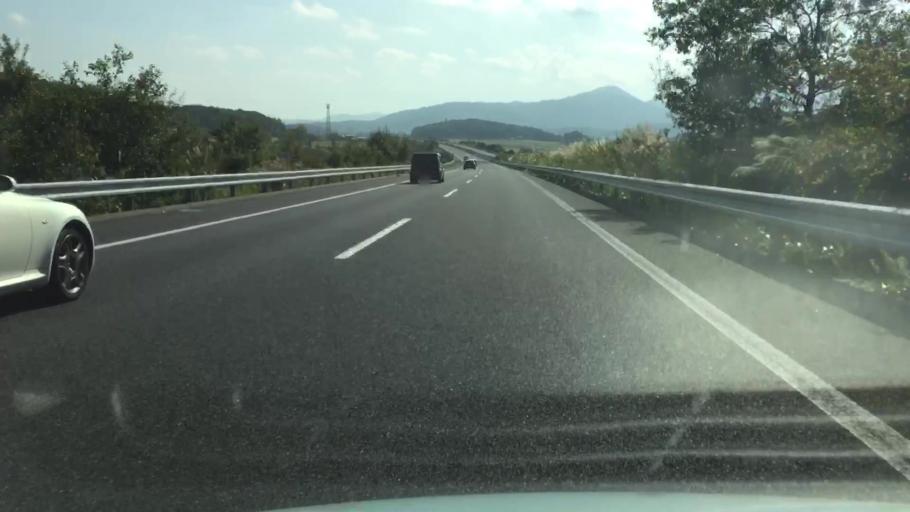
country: JP
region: Ibaraki
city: Iwase
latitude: 36.3675
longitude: 140.0544
